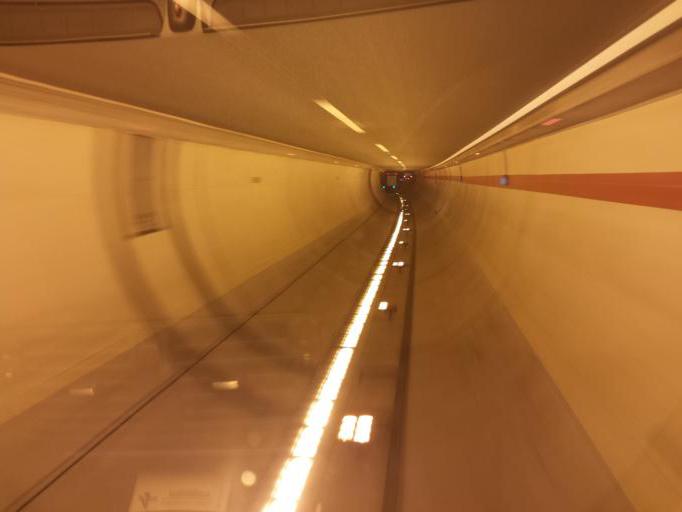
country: HR
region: Primorsko-Goranska
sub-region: Grad Delnice
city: Delnice
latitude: 45.3645
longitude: 14.7692
